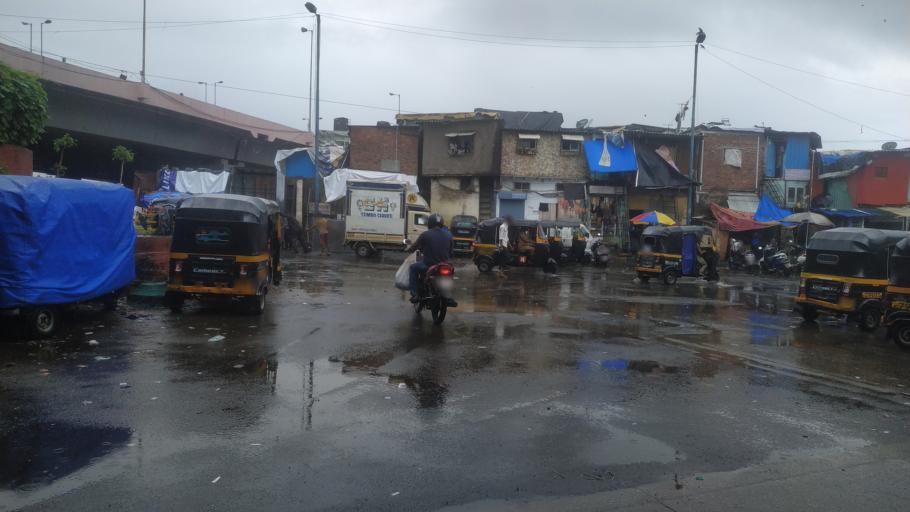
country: IN
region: Maharashtra
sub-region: Mumbai Suburban
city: Mumbai
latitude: 19.0503
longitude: 72.8370
